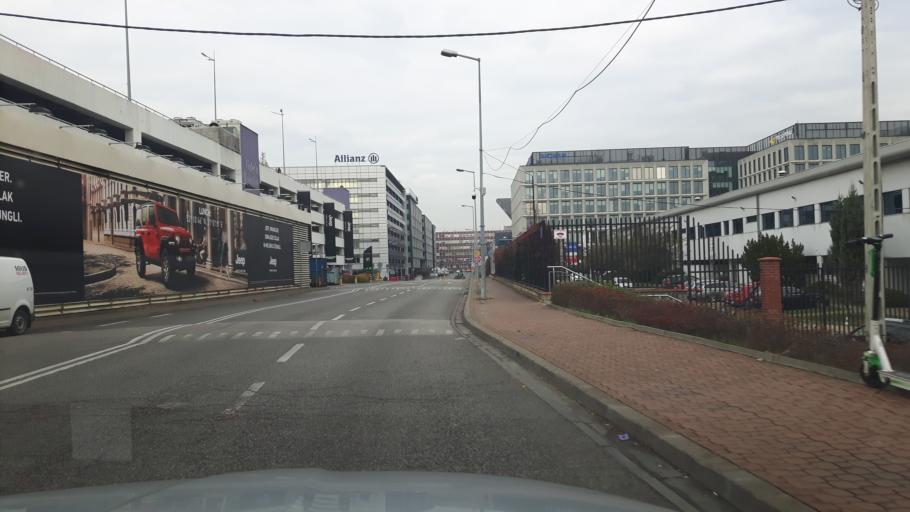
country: PL
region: Masovian Voivodeship
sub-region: Warszawa
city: Mokotow
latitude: 52.1796
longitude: 21.0062
